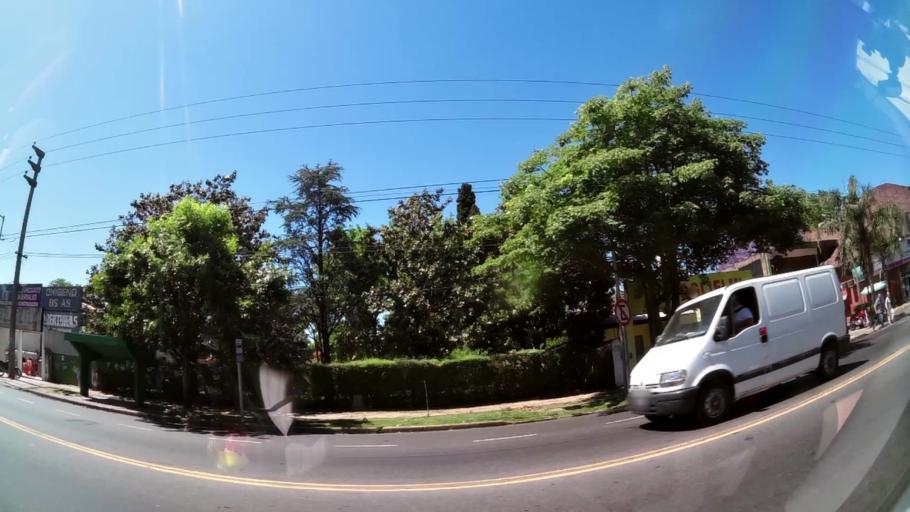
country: AR
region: Buenos Aires
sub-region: Partido de Tigre
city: Tigre
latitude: -34.4915
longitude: -58.6267
